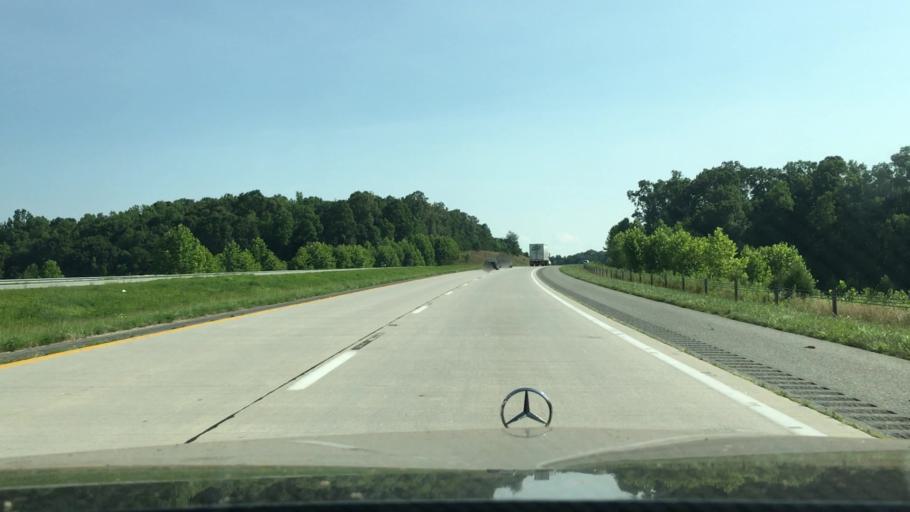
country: US
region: Virginia
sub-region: Amherst County
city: Madison Heights
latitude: 37.4785
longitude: -79.0767
